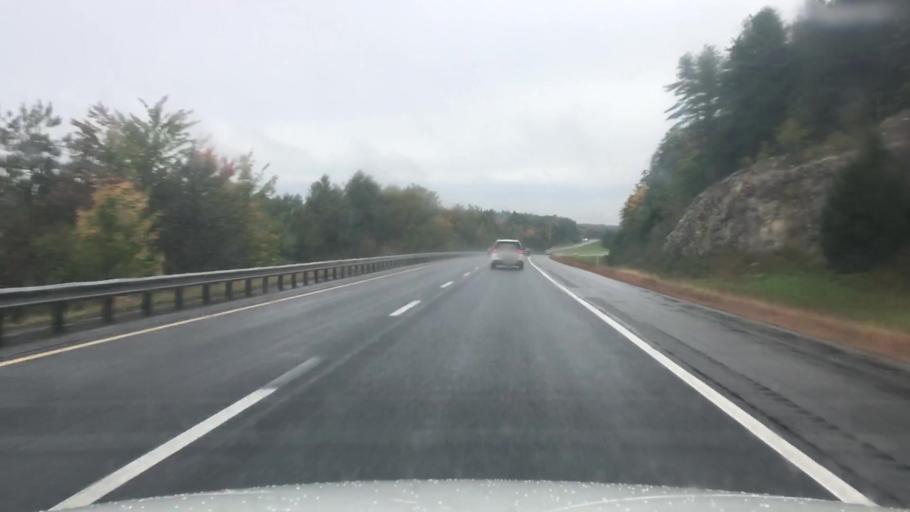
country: US
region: Maine
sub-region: Sagadahoc County
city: Topsham
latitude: 43.9776
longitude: -69.9455
